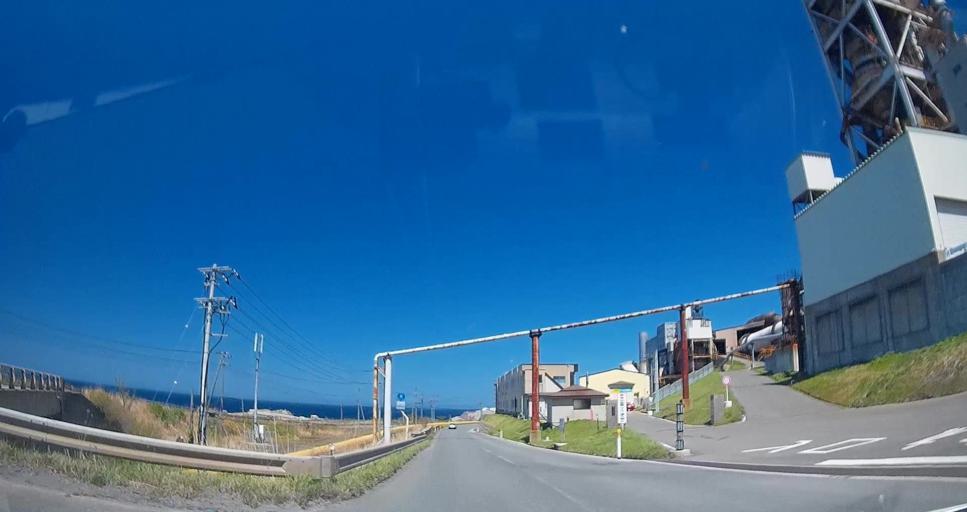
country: JP
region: Aomori
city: Mutsu
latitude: 41.4063
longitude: 141.4356
